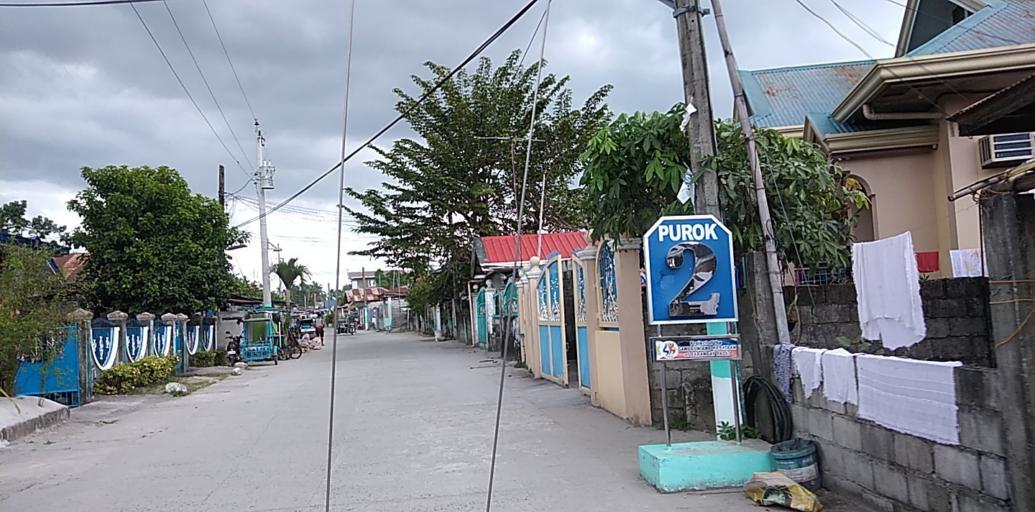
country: PH
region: Central Luzon
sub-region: Province of Pampanga
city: Pio
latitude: 15.0455
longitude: 120.5381
